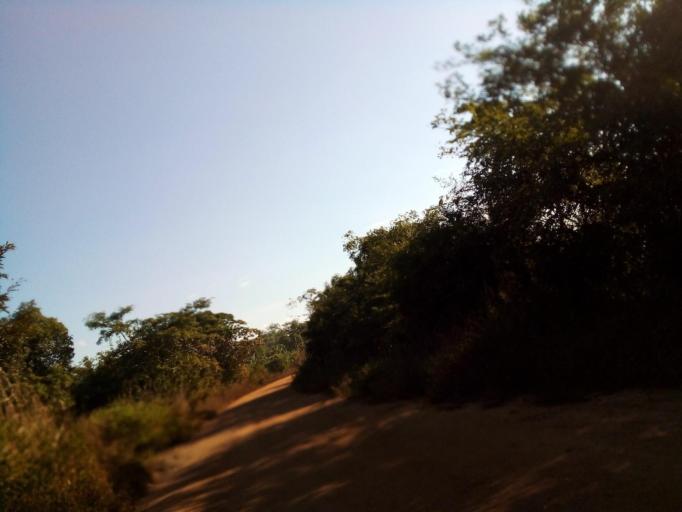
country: MZ
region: Zambezia
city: Quelimane
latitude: -17.4871
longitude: 36.5547
